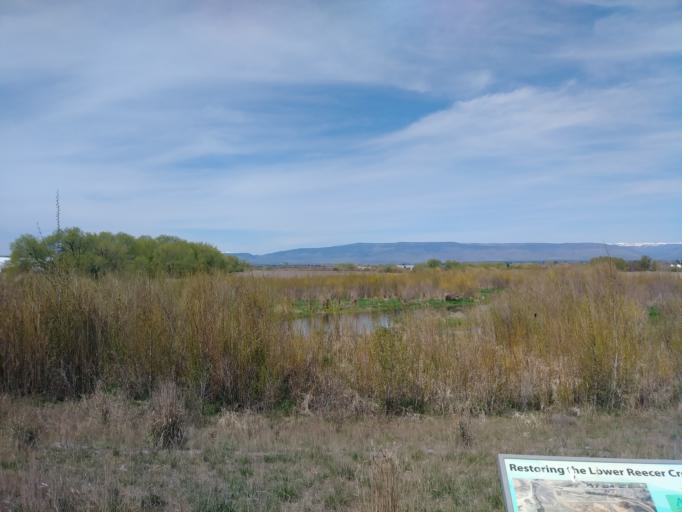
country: US
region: Washington
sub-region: Kittitas County
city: Ellensburg
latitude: 46.9910
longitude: -120.5714
